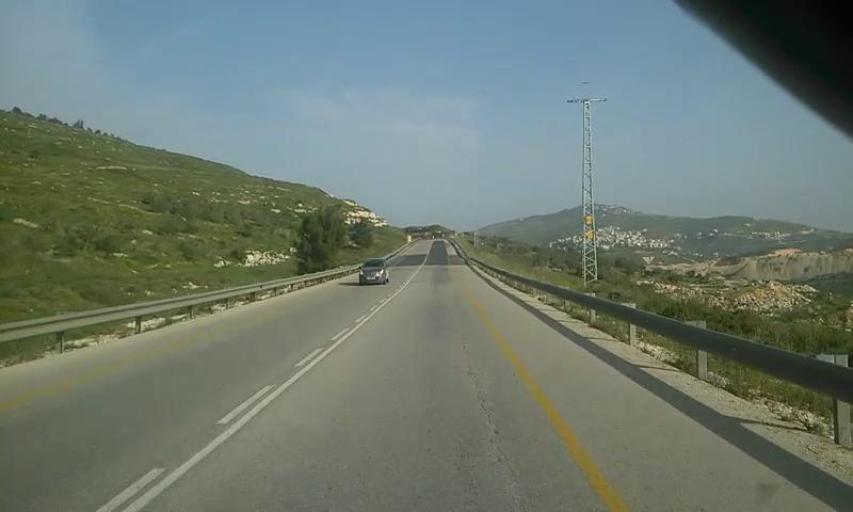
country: PS
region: West Bank
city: Sarrah
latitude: 32.1920
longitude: 35.1934
